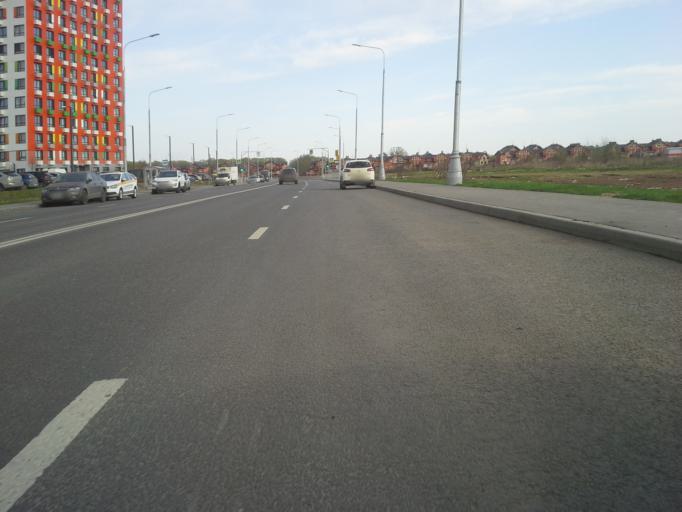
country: RU
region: Moskovskaya
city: Kommunarka
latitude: 55.5415
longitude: 37.4784
